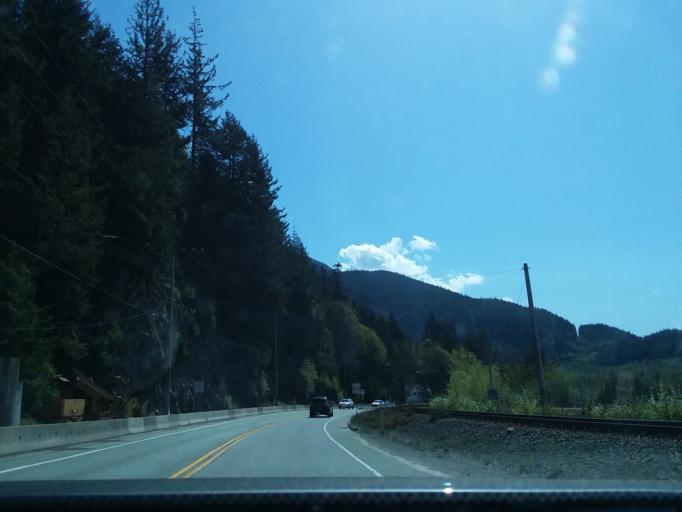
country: CA
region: British Columbia
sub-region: Greater Vancouver Regional District
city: Lions Bay
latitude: 49.6222
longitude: -123.2054
